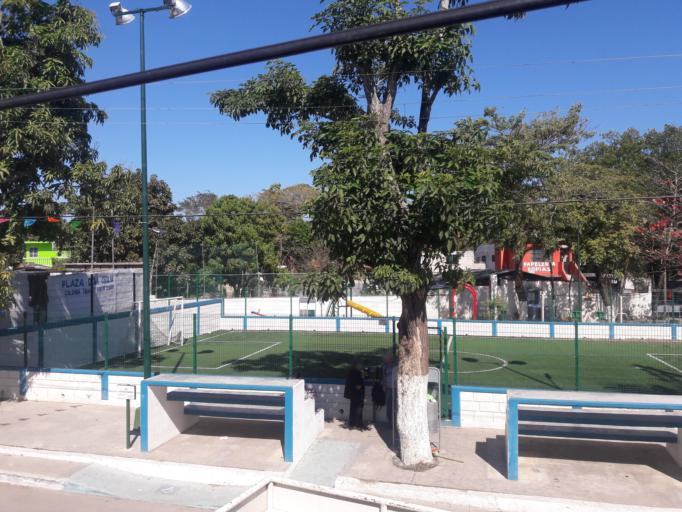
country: MX
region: Tamaulipas
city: Ciudad Madero
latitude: 22.2405
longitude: -97.8339
